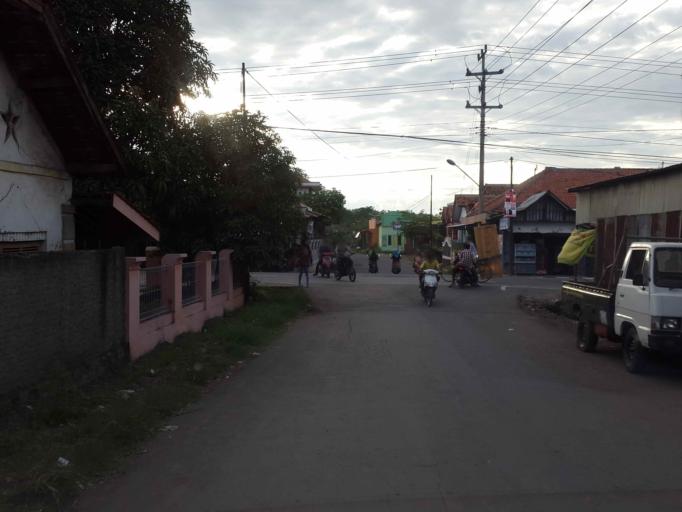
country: ID
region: Central Java
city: Ketanggungan
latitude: -6.9326
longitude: 108.8927
